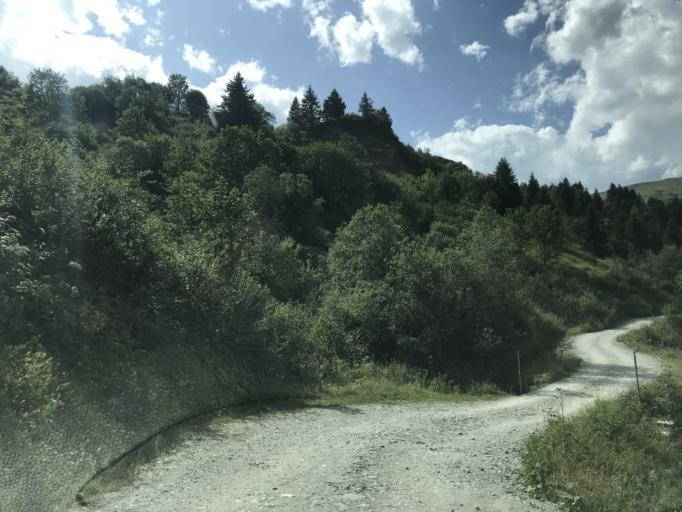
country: FR
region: Rhone-Alpes
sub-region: Departement de la Savoie
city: Beaufort
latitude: 45.6624
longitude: 6.6223
